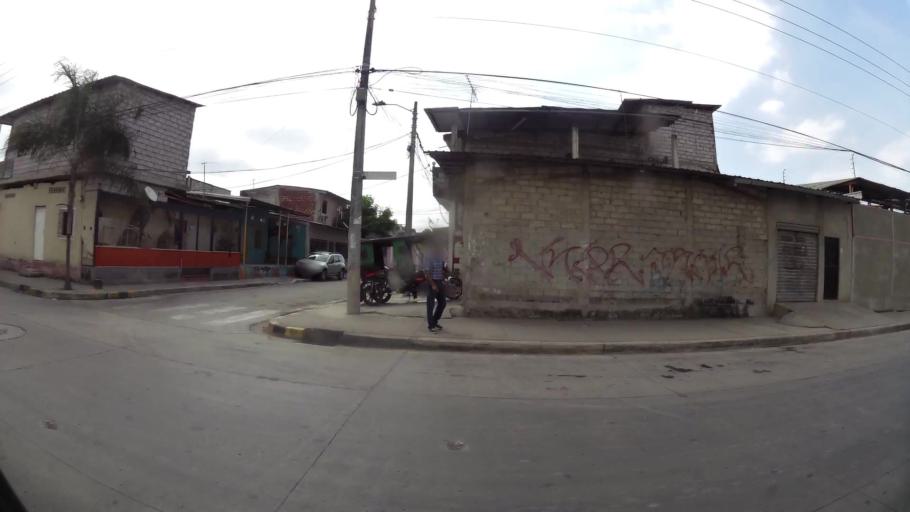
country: EC
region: Guayas
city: Santa Lucia
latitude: -2.0893
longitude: -79.9332
